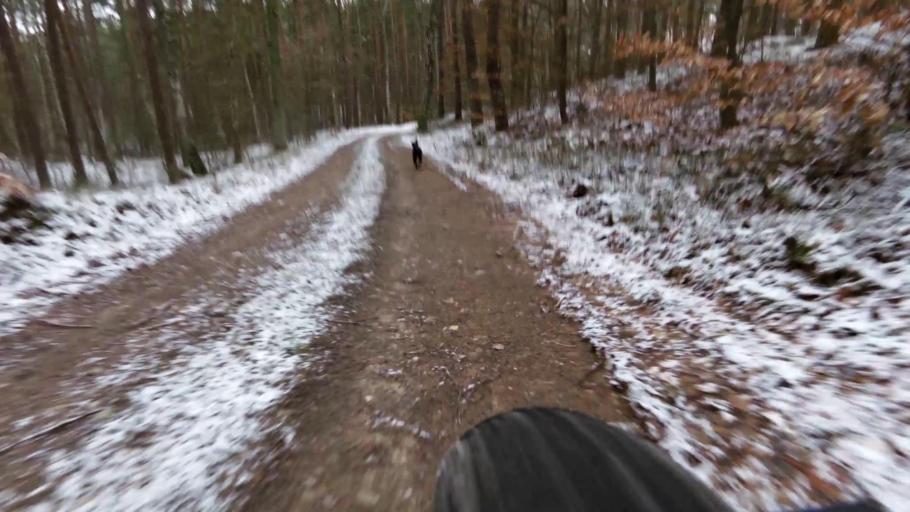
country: PL
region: West Pomeranian Voivodeship
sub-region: Powiat walecki
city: Miroslawiec
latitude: 53.3304
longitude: 16.1026
